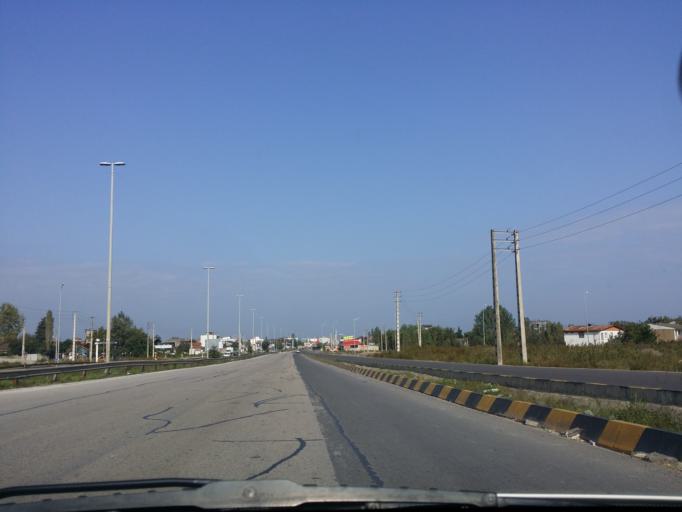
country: IR
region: Mazandaran
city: Chalus
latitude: 36.6552
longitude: 51.4031
